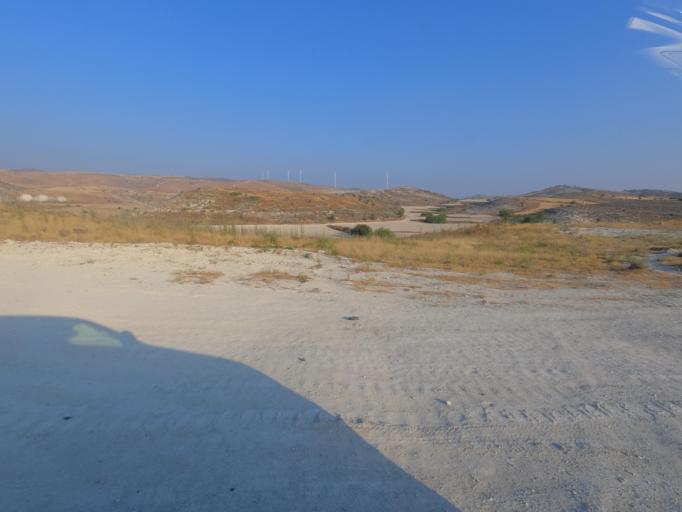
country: CY
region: Larnaka
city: Psevdas
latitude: 34.9206
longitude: 33.5135
